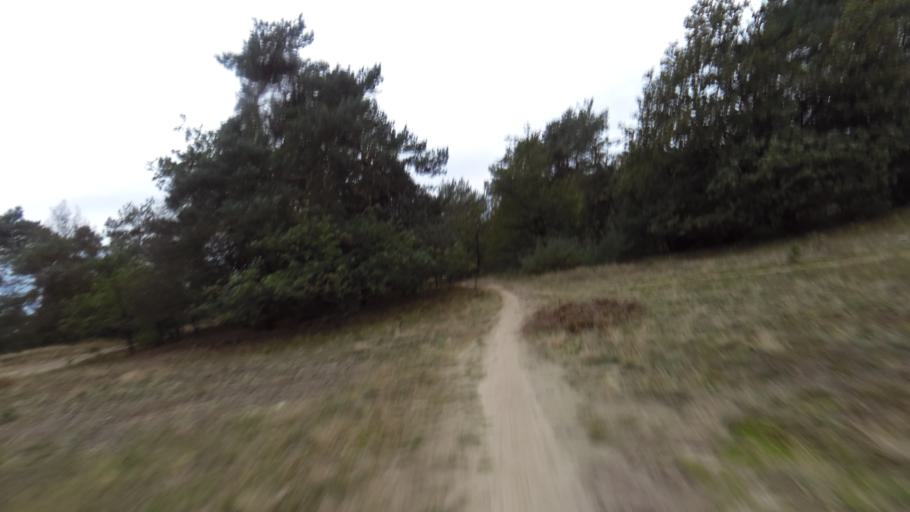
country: NL
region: Gelderland
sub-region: Gemeente Ede
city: Harskamp
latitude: 52.1873
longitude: 5.7999
